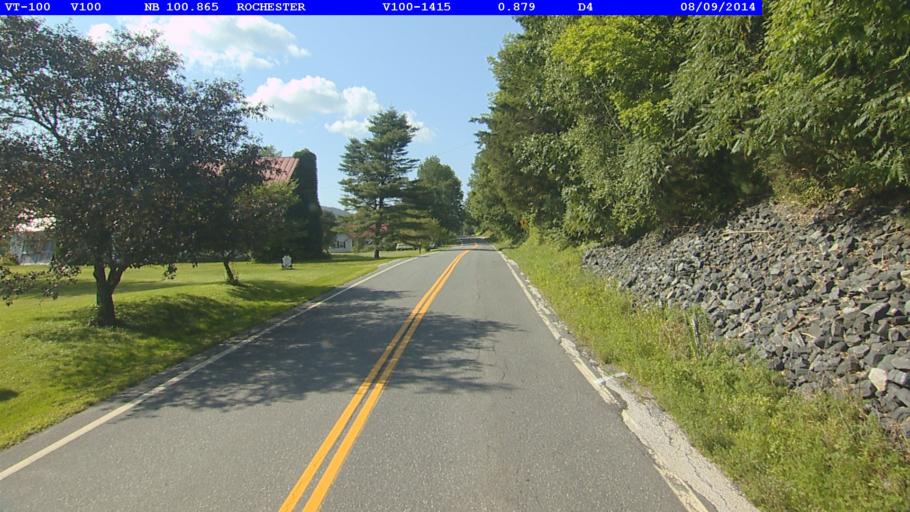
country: US
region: Vermont
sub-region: Orange County
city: Randolph
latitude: 43.8163
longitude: -72.7861
